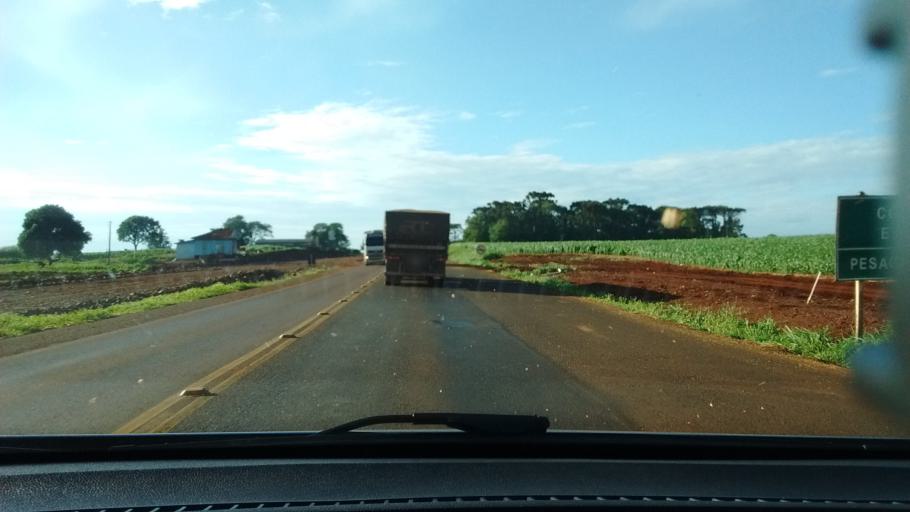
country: BR
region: Parana
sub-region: Cascavel
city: Cascavel
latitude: -25.1767
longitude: -53.6029
